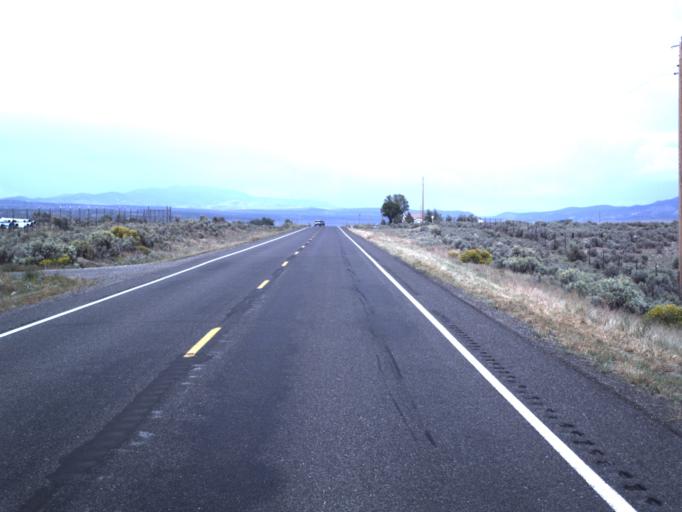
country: US
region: Utah
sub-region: Garfield County
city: Panguitch
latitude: 37.9088
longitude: -112.4295
